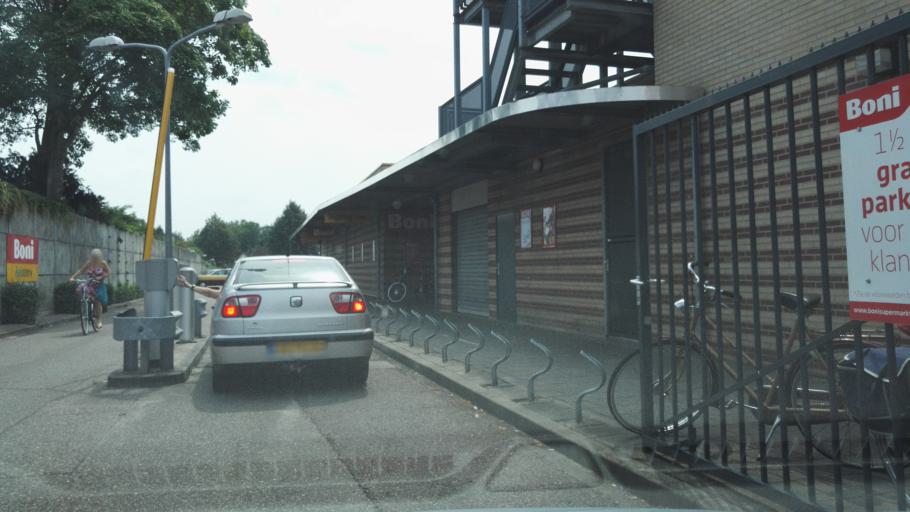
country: NL
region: Gelderland
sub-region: Gemeente Apeldoorn
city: Apeldoorn
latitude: 52.2124
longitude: 5.9542
